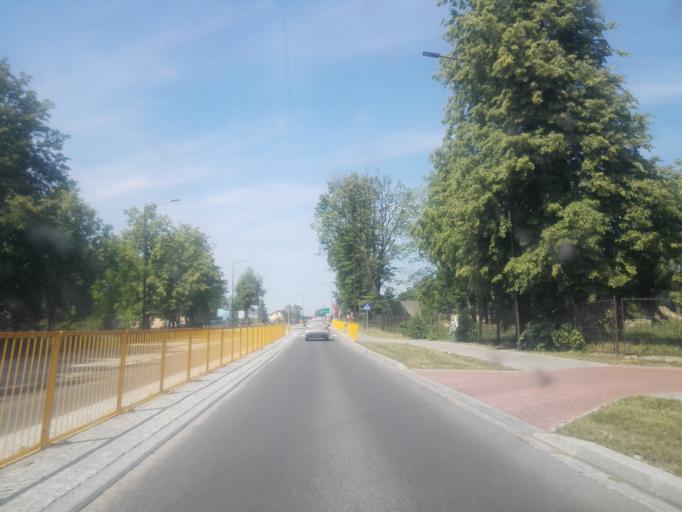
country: PL
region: Podlasie
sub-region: Powiat sejnenski
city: Sejny
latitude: 54.1086
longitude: 23.3396
